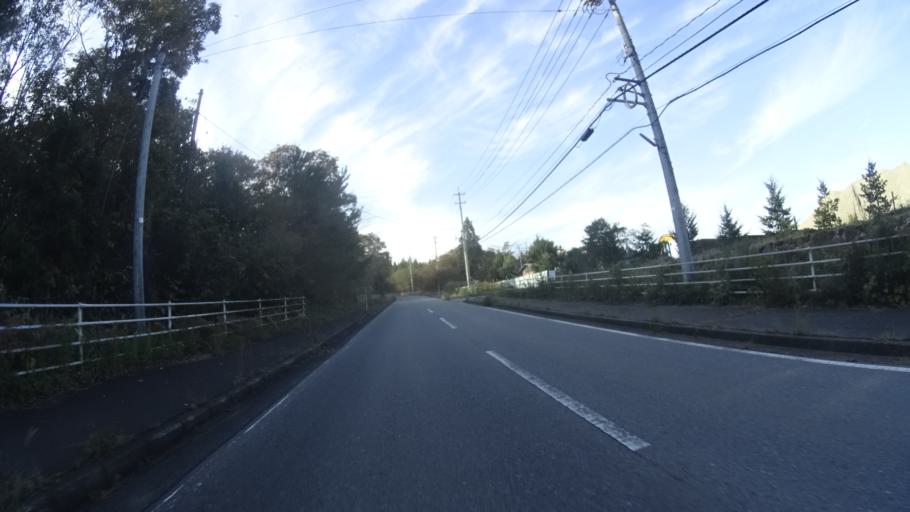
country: JP
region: Ishikawa
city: Hakui
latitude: 37.0659
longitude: 136.7663
